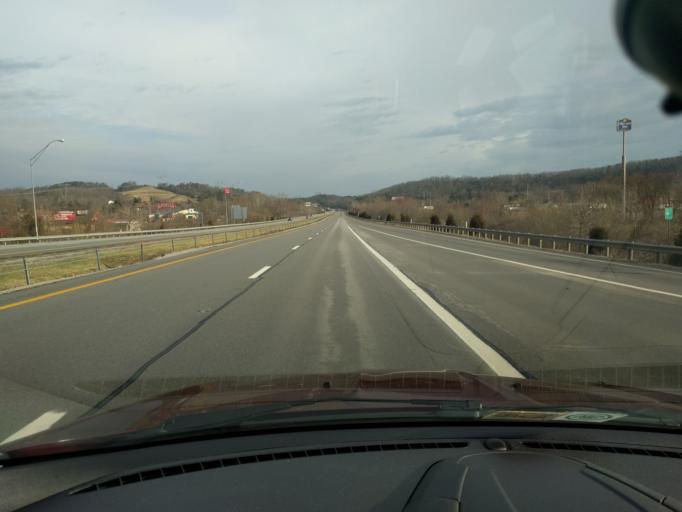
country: US
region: West Virginia
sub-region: Jackson County
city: Ripley
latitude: 38.8219
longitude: -81.7273
